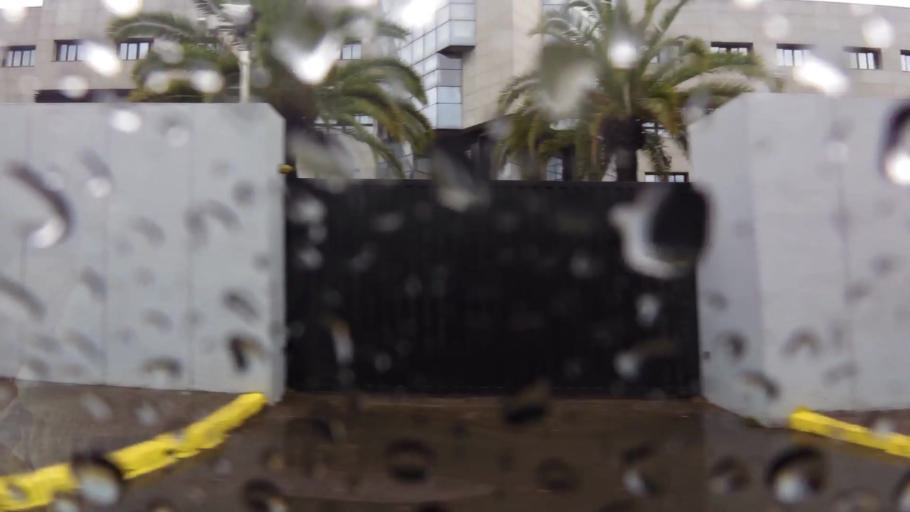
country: MA
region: Grand Casablanca
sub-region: Casablanca
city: Casablanca
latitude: 33.5560
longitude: -7.6669
